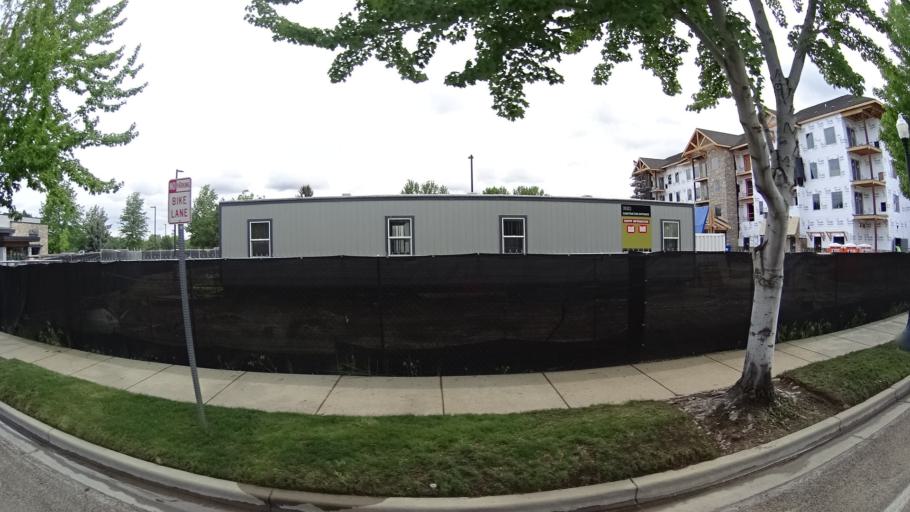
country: US
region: Idaho
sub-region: Ada County
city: Eagle
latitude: 43.6890
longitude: -116.3456
